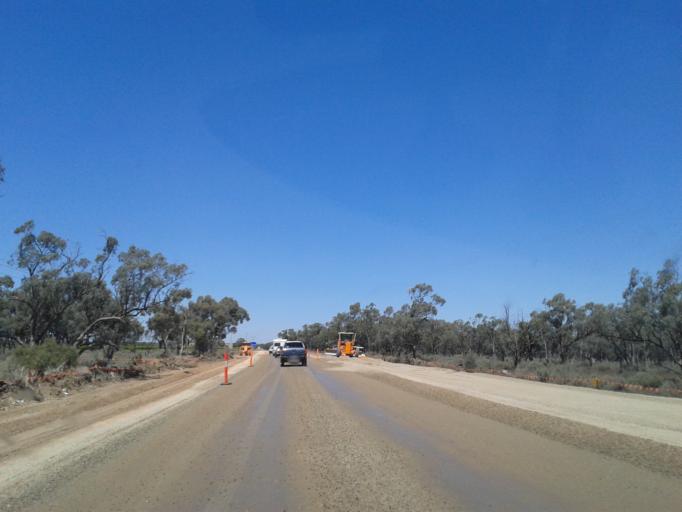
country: AU
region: New South Wales
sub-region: Wentworth
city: Gol Gol
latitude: -34.5636
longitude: 142.7265
